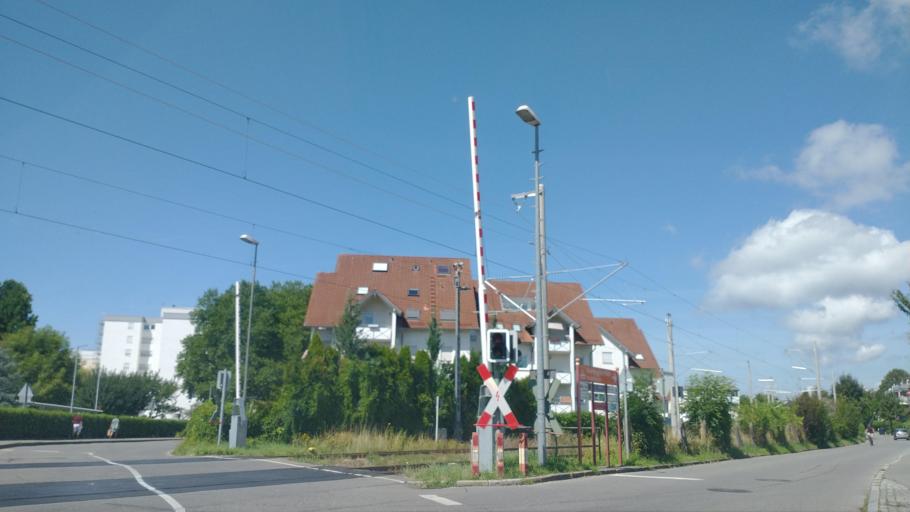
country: DE
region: Baden-Wuerttemberg
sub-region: Tuebingen Region
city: Kressbronn am Bodensee
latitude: 47.5970
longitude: 9.5953
